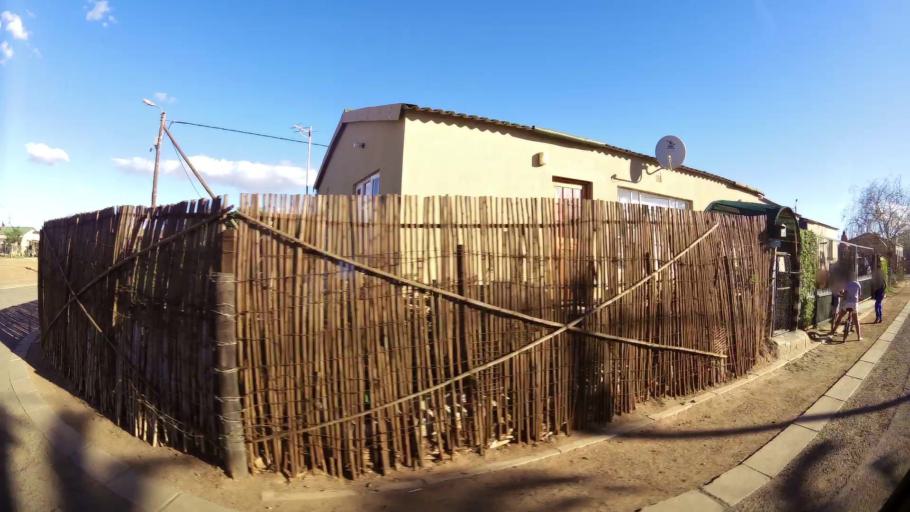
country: ZA
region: Western Cape
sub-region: Eden District Municipality
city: Riversdale
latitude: -34.1063
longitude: 20.9630
